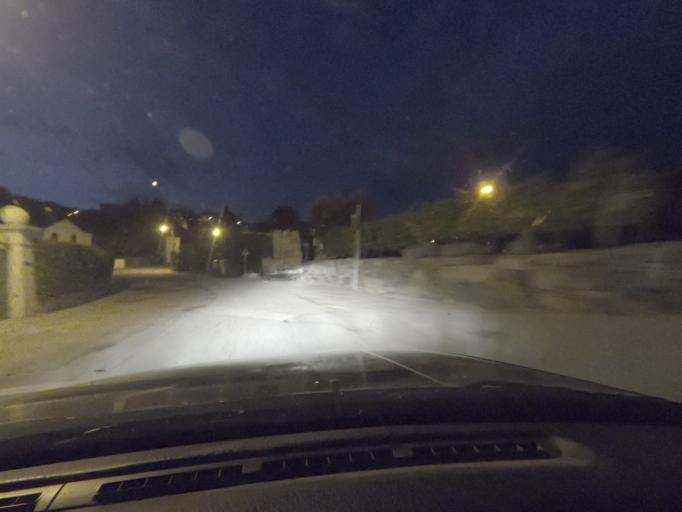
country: PT
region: Vila Real
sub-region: Mesao Frio
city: Mesao Frio
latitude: 41.1996
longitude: -7.8487
